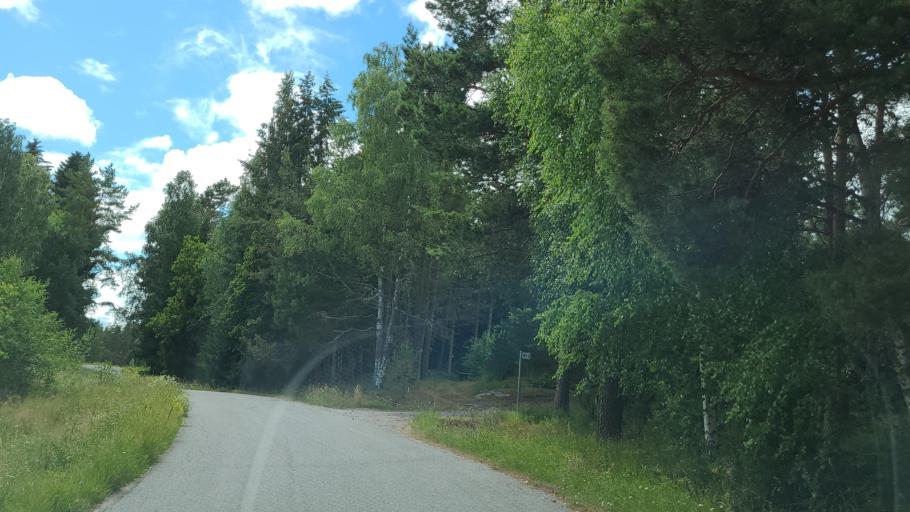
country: FI
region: Varsinais-Suomi
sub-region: Aboland-Turunmaa
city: Nagu
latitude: 60.1647
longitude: 22.0323
